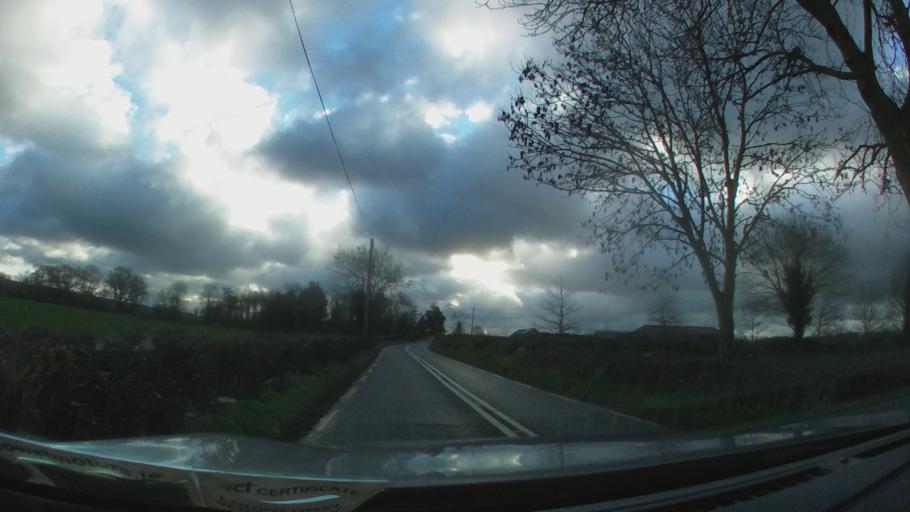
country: IE
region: Leinster
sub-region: Kilkenny
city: Thomastown
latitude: 52.5670
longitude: -7.1171
